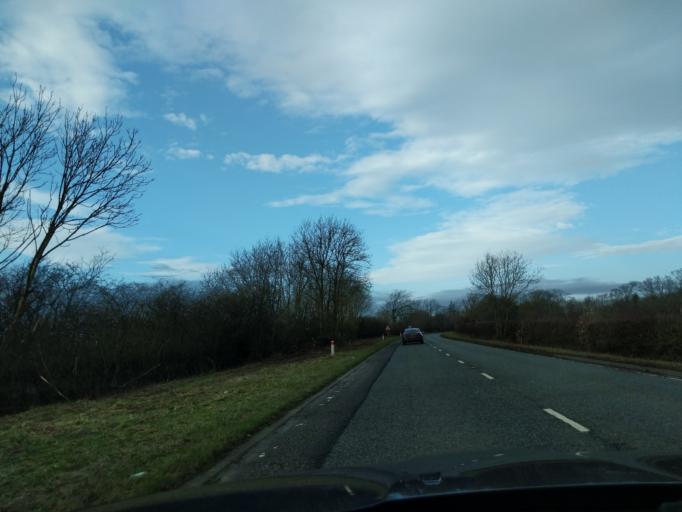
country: GB
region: England
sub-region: Northumberland
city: Darras Hall
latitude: 55.0687
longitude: -1.7886
